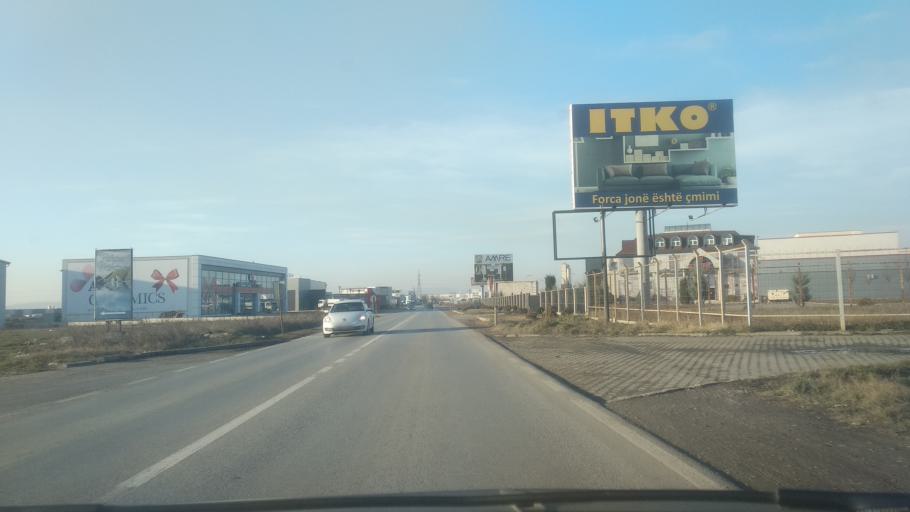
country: XK
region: Pristina
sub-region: Lipjan
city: Lipljan
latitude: 42.5585
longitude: 21.1372
